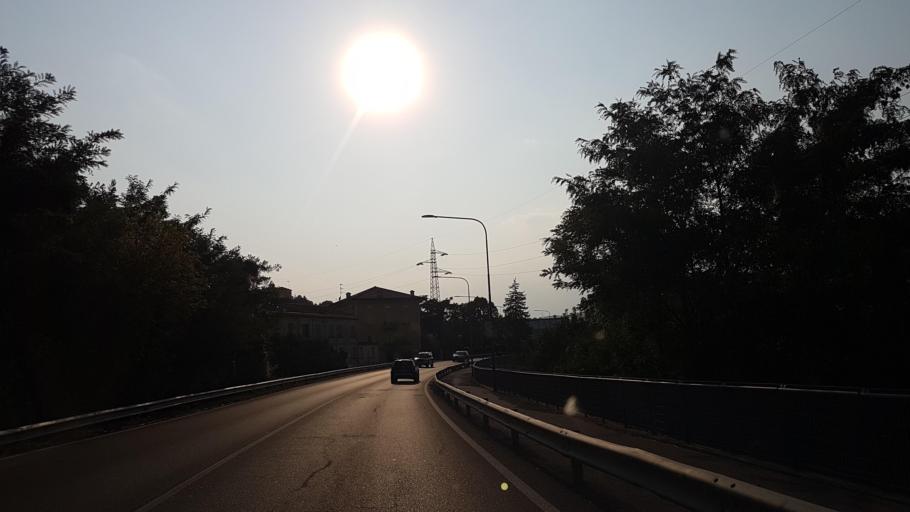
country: IT
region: Emilia-Romagna
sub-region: Provincia di Parma
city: Ricco
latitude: 44.7010
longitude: 10.1223
